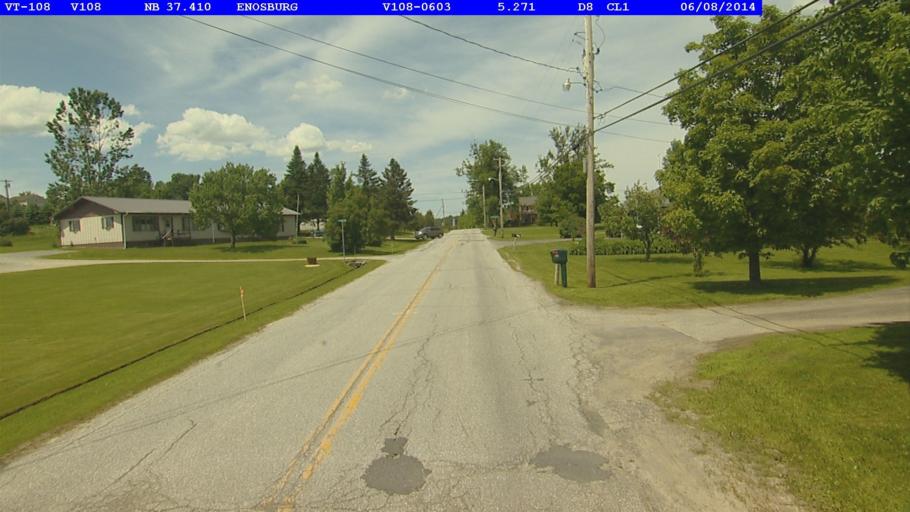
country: US
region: Vermont
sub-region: Franklin County
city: Enosburg Falls
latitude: 44.9163
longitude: -72.8055
